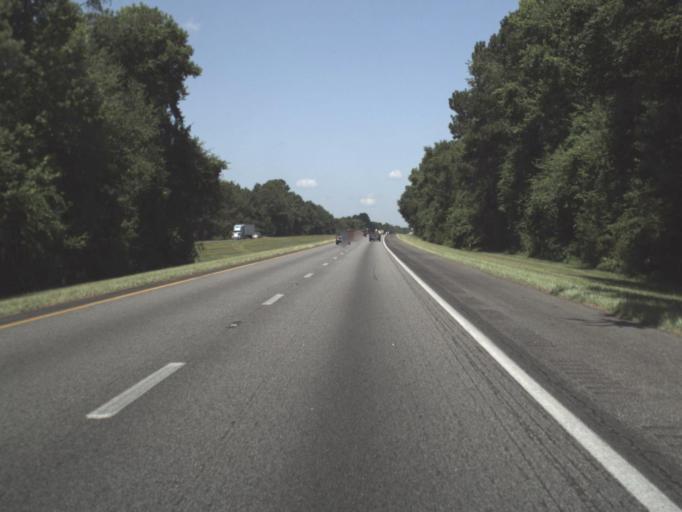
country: US
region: Florida
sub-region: Madison County
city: Madison
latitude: 30.4305
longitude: -83.5646
